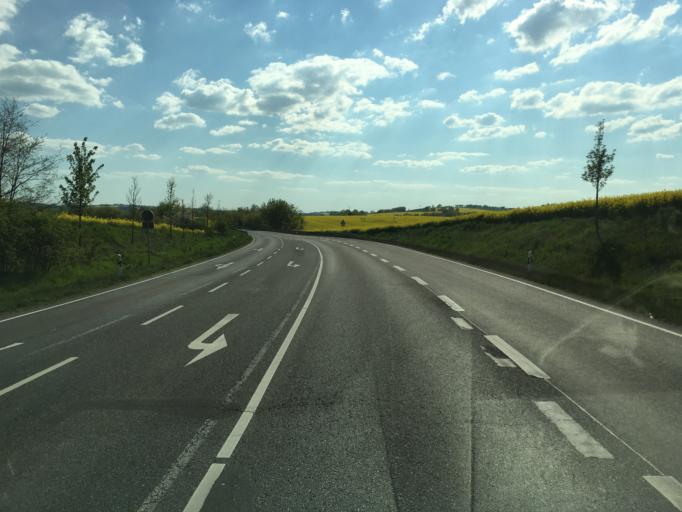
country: DE
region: Saxony
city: Dobeln
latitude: 51.1454
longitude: 13.1096
